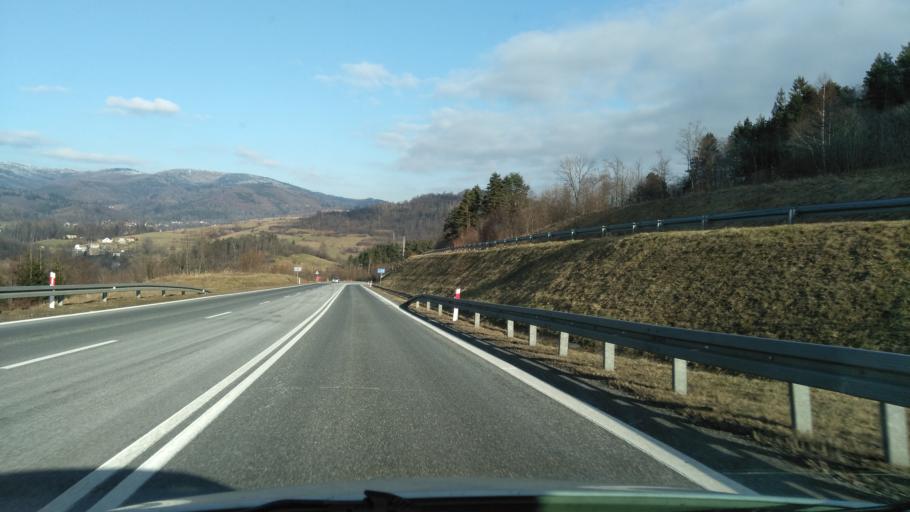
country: PL
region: Silesian Voivodeship
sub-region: Powiat zywiecki
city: Milowka
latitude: 49.5595
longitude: 19.0620
